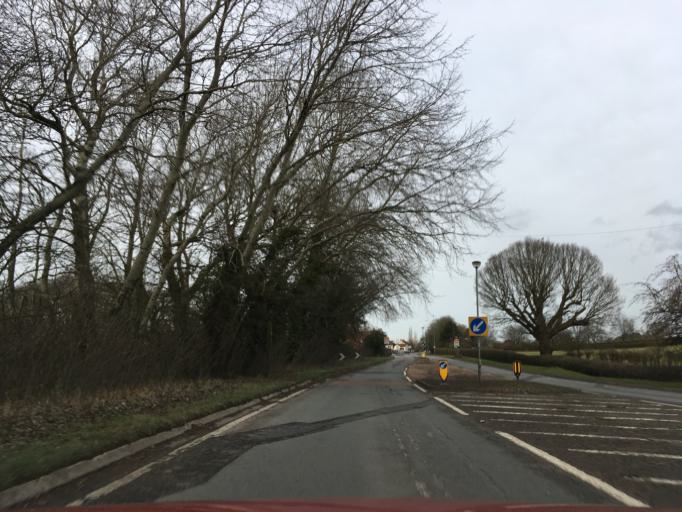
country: GB
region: England
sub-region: South Gloucestershire
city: Falfield
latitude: 51.6330
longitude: -2.4612
